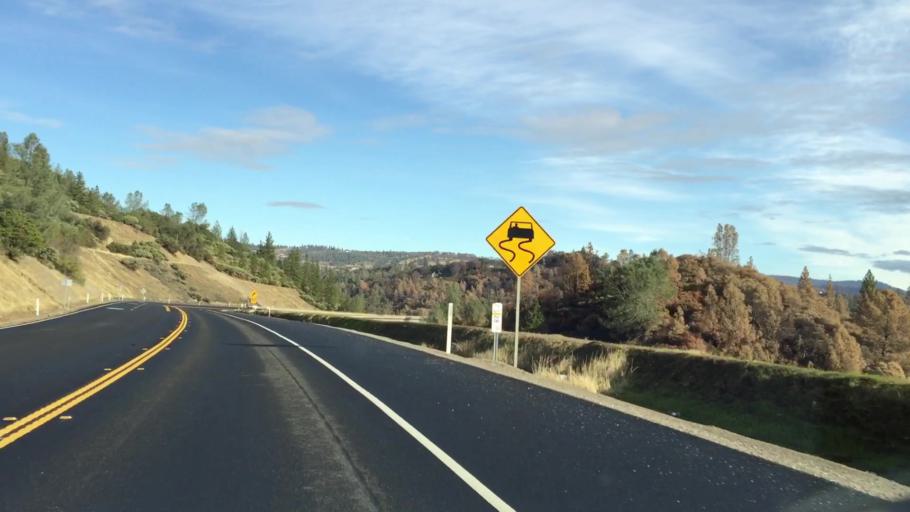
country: US
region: California
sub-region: Butte County
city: Paradise
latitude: 39.6593
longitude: -121.5357
